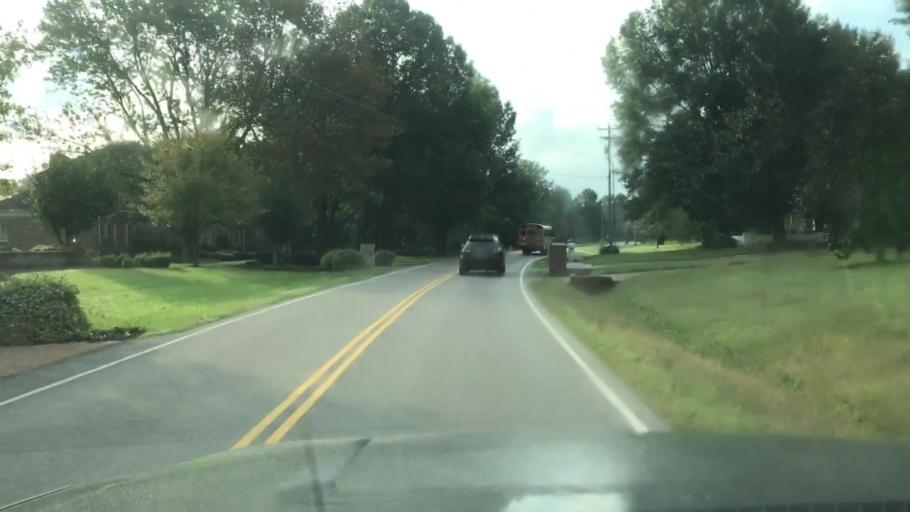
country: US
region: Tennessee
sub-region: Davidson County
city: Forest Hills
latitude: 36.0295
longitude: -86.8304
